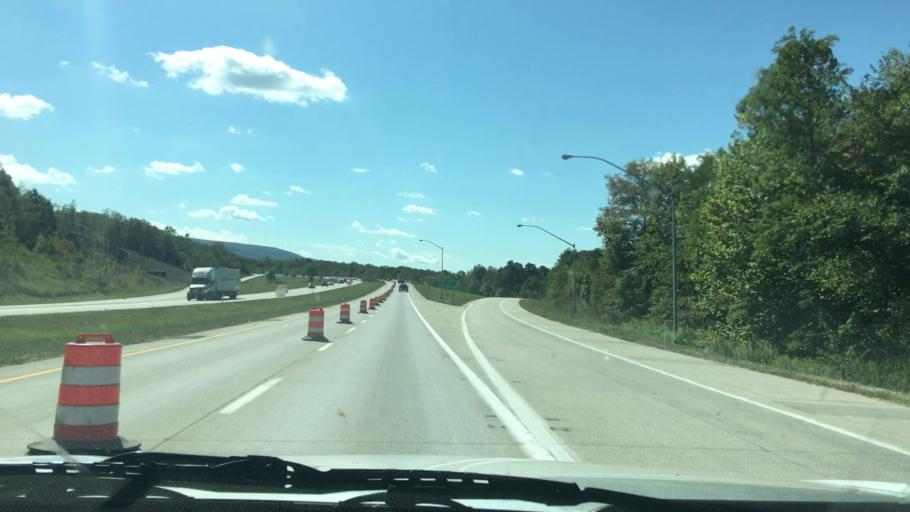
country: US
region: Pennsylvania
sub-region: Blair County
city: Bellwood
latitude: 40.6034
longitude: -78.3123
